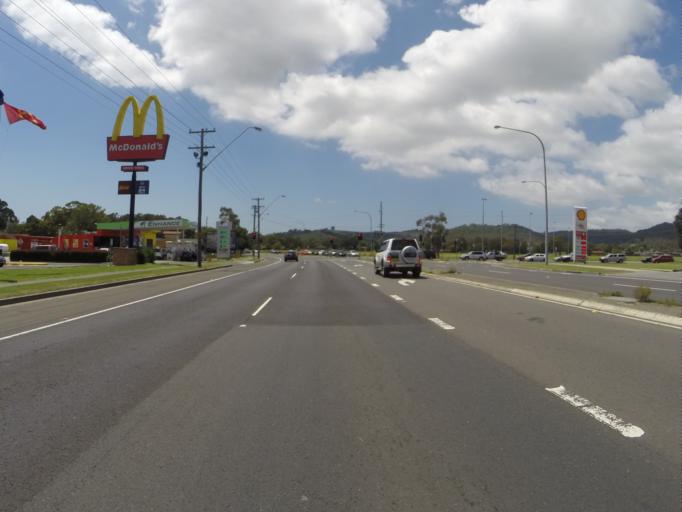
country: AU
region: New South Wales
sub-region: Shellharbour
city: Albion Park Rail
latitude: -34.5674
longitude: 150.8023
